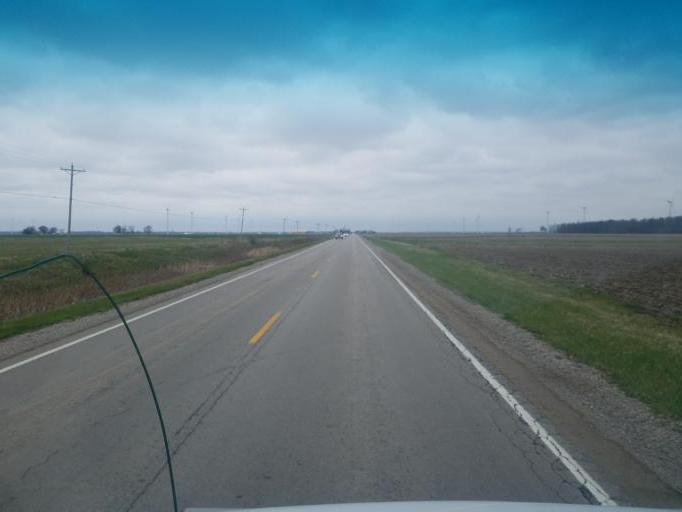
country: US
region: Ohio
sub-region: Van Wert County
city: Convoy
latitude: 40.9941
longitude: -84.7265
